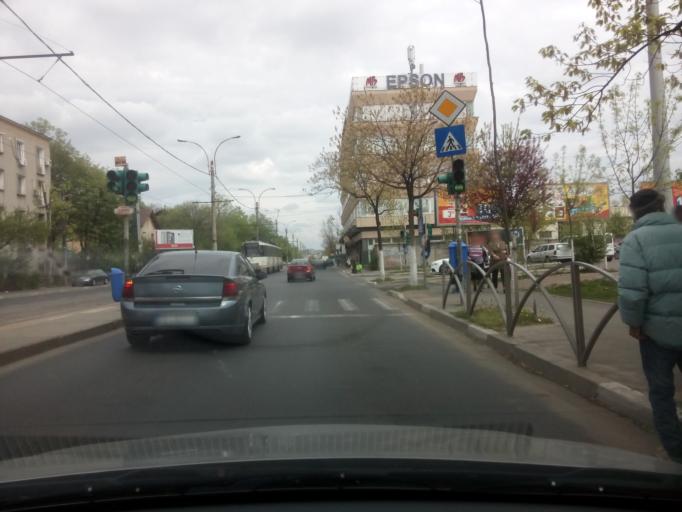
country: RO
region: Bucuresti
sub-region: Municipiul Bucuresti
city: Bucharest
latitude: 44.4643
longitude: 26.1083
